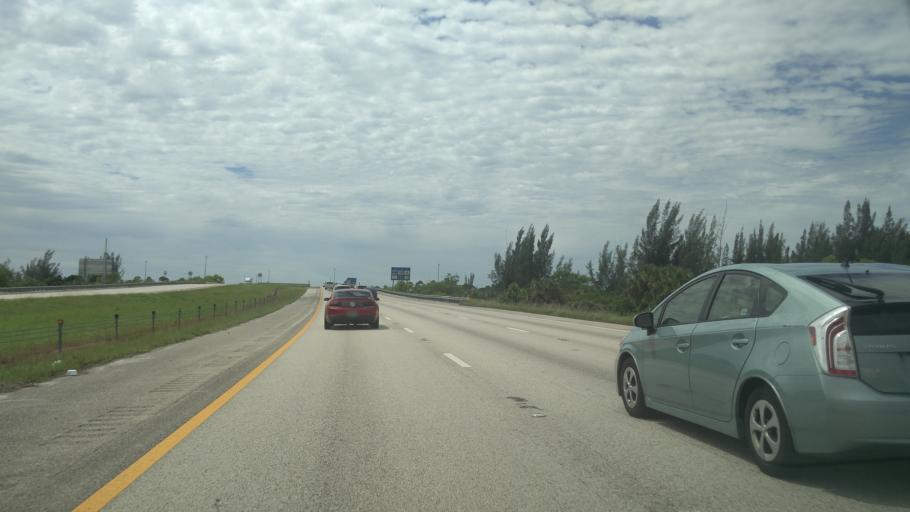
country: US
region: Florida
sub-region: Charlotte County
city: Punta Gorda
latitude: 26.9460
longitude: -82.0207
